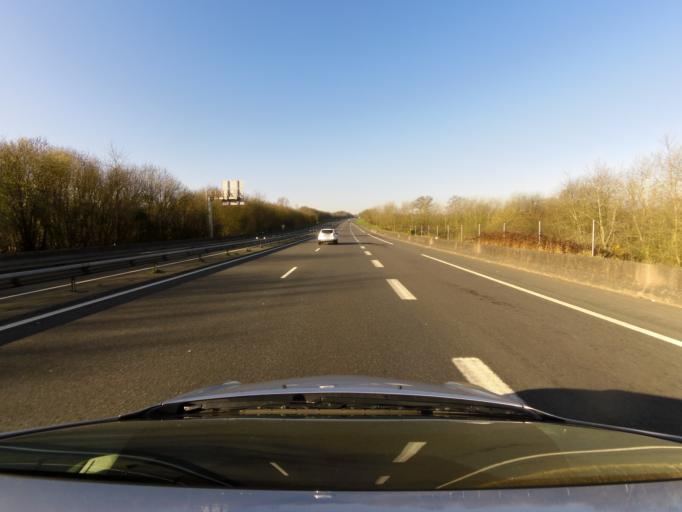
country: FR
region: Lower Normandy
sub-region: Departement du Calvados
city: Saint-Martin-des-Besaces
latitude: 49.0233
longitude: -0.8364
